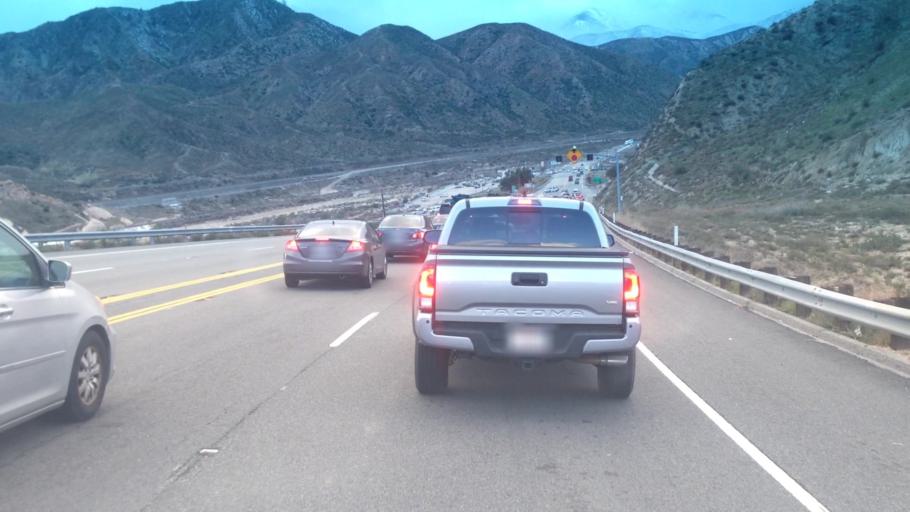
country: US
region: California
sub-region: San Bernardino County
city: Oak Hills
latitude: 34.3122
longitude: -117.4698
